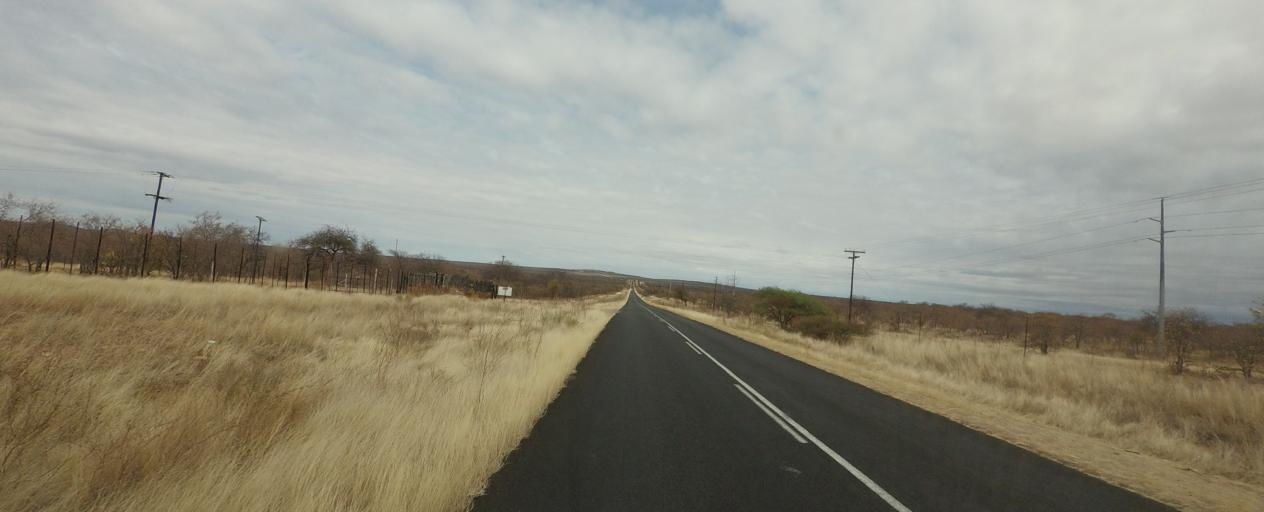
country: ZW
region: Matabeleland South
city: Beitbridge
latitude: -22.4306
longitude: 29.4486
